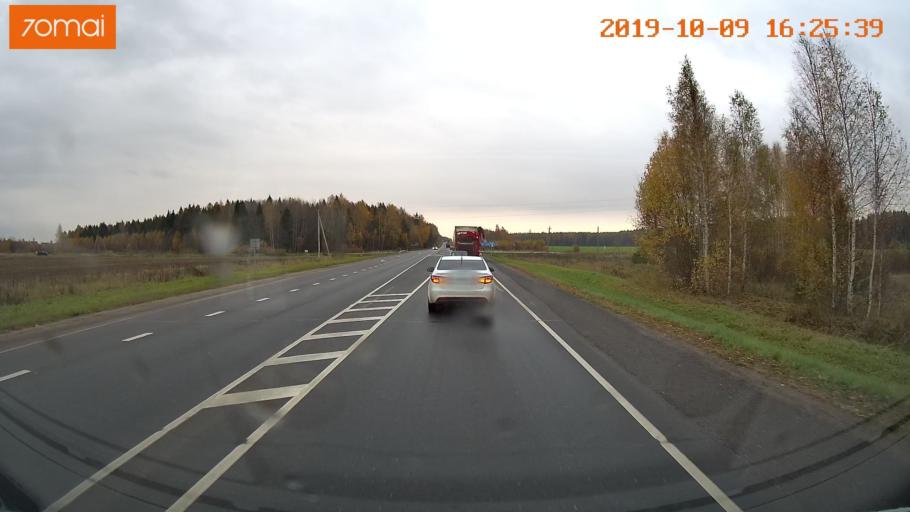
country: RU
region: Kostroma
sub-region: Kostromskoy Rayon
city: Kostroma
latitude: 57.6413
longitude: 40.9207
